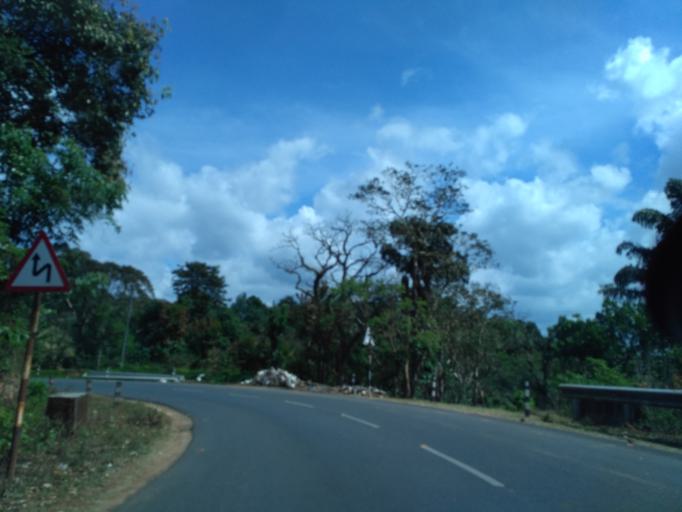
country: IN
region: Karnataka
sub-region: Kodagu
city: Madikeri
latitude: 12.4168
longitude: 75.7101
